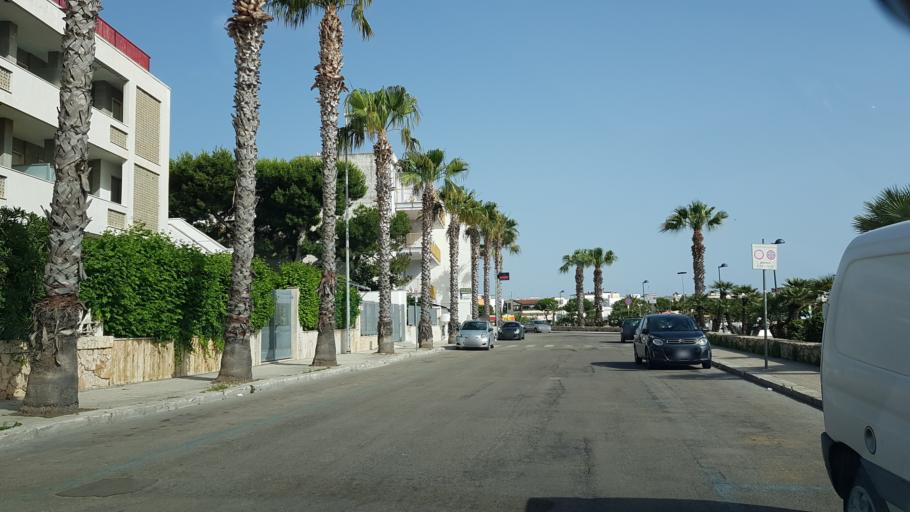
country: IT
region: Apulia
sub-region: Provincia di Lecce
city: Porto Cesareo
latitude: 40.2610
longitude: 17.8901
